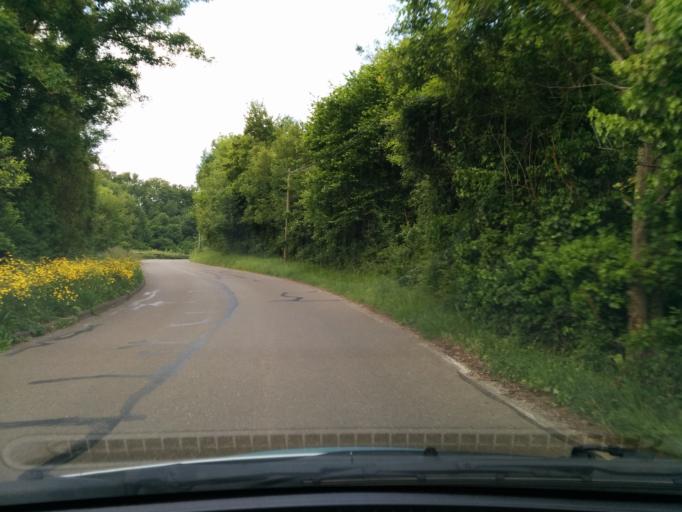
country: FR
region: Ile-de-France
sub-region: Departement des Yvelines
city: Oinville-sur-Montcient
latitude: 49.0263
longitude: 1.8178
